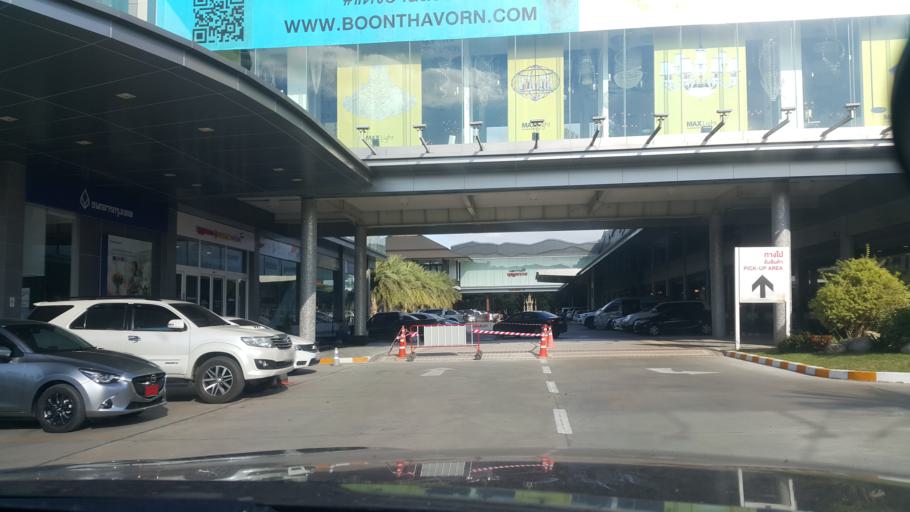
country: TH
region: Chiang Mai
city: Saraphi
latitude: 18.7453
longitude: 99.0350
